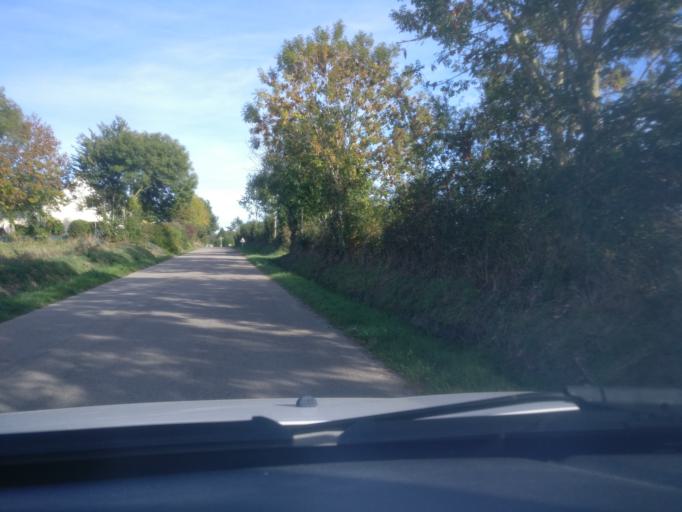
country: FR
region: Lower Normandy
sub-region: Departement de la Manche
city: Marcey-les-Greves
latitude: 48.6997
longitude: -1.4361
